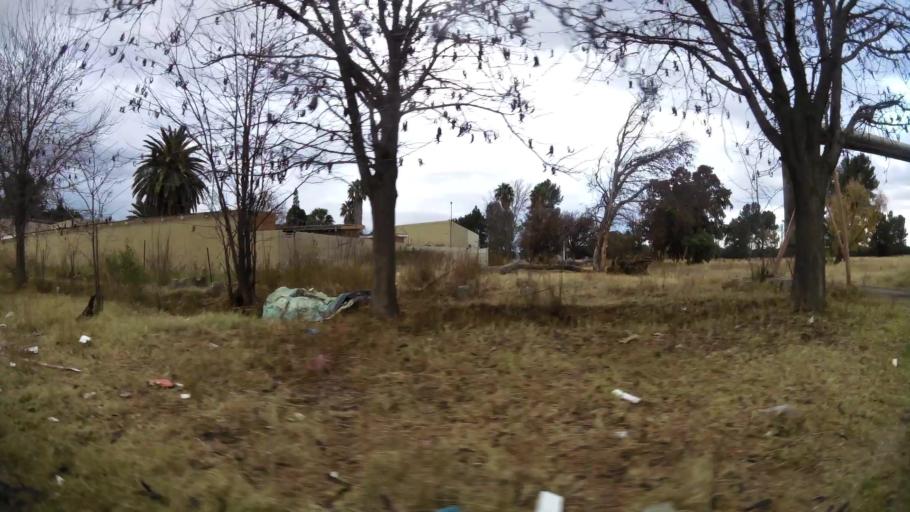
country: ZA
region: Orange Free State
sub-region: Lejweleputswa District Municipality
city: Welkom
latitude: -27.9633
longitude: 26.7155
